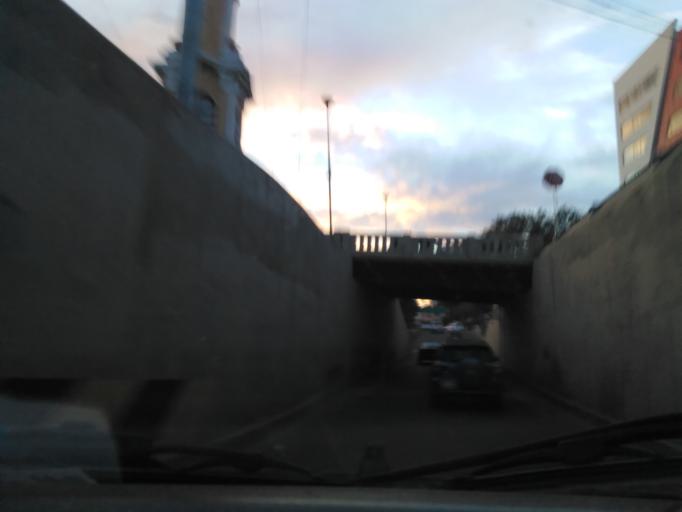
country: BO
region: Cochabamba
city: Cochabamba
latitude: -17.3803
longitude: -66.1568
